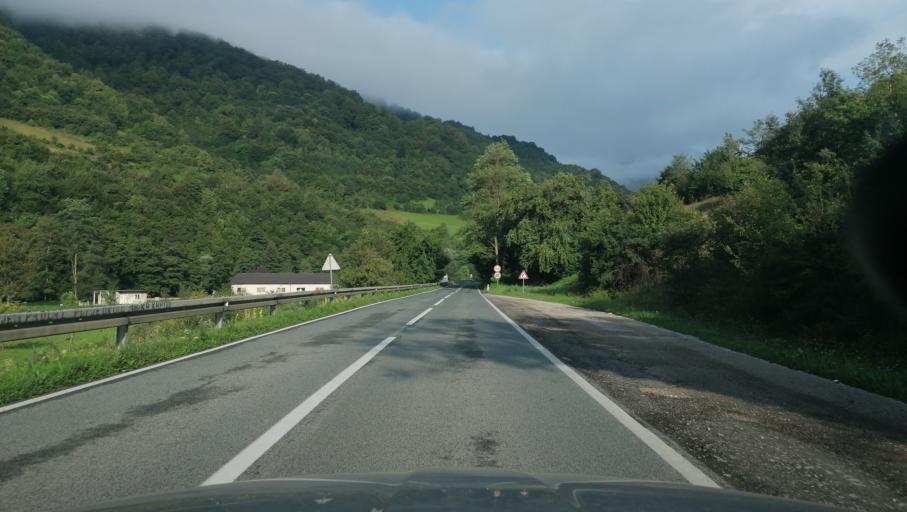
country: BA
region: Federation of Bosnia and Herzegovina
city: Jajce
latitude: 44.2795
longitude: 17.2663
